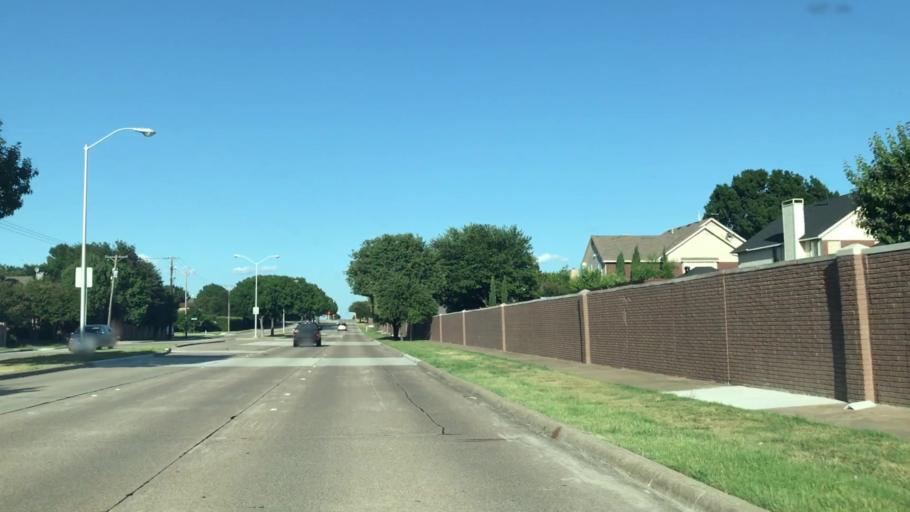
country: US
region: Texas
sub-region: Collin County
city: Plano
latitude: 33.0714
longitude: -96.7311
